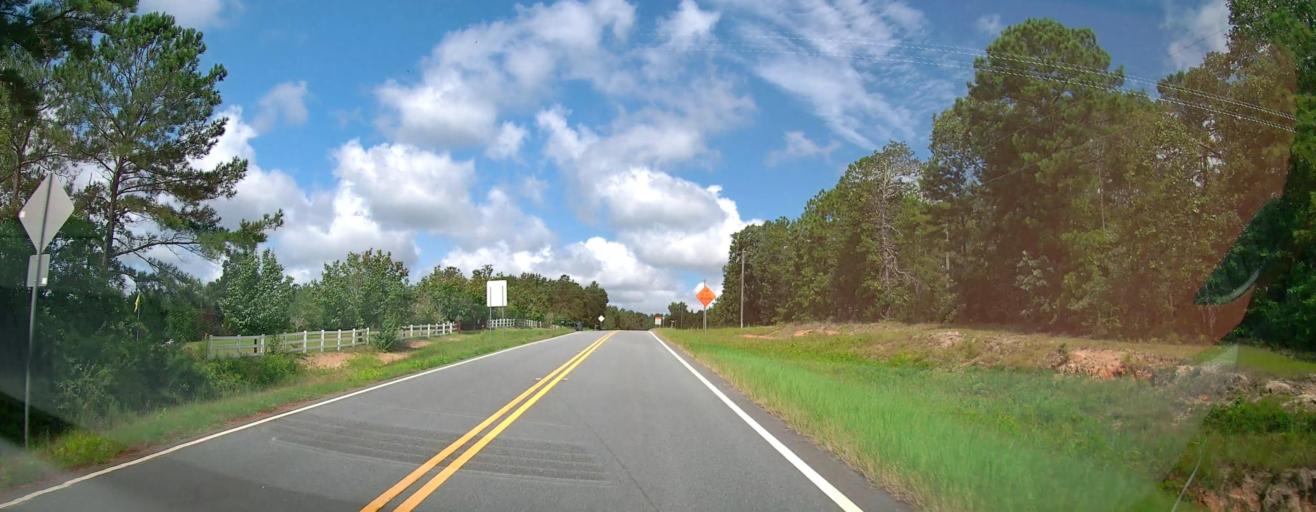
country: US
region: Georgia
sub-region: Crawford County
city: Knoxville
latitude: 32.6979
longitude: -83.9234
